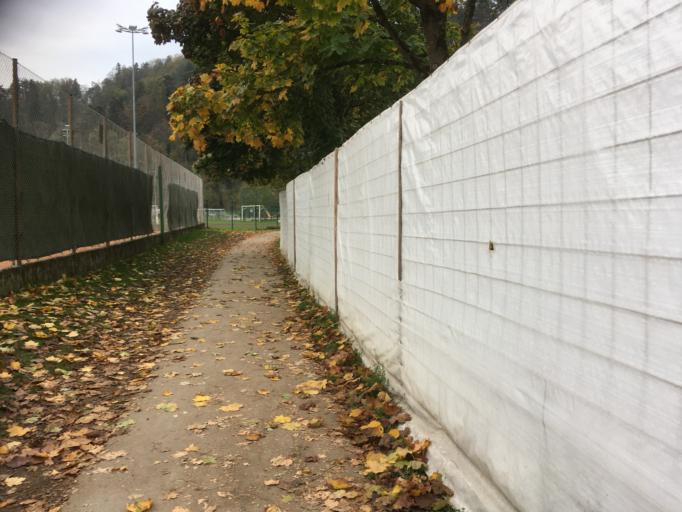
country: SI
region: Menges
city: Menges
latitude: 46.1654
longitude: 14.5694
